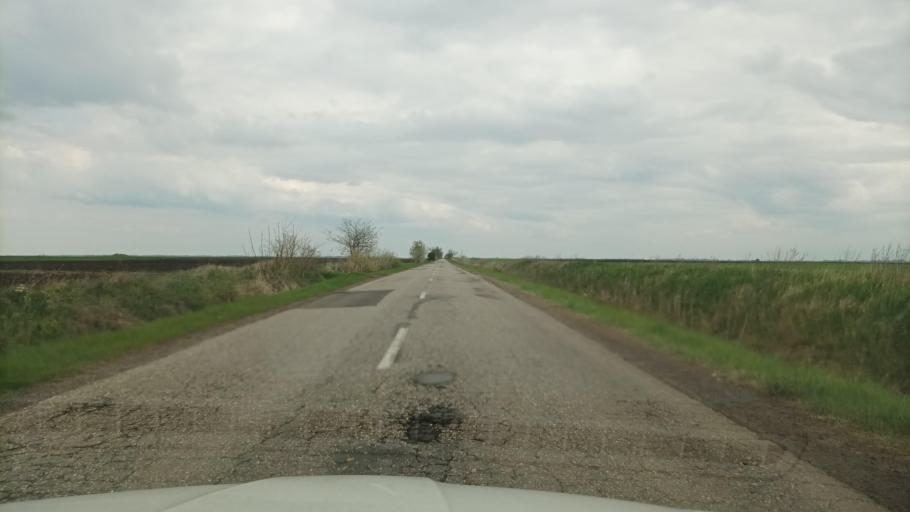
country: HU
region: Pest
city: Tortel
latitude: 47.1287
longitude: 19.9458
